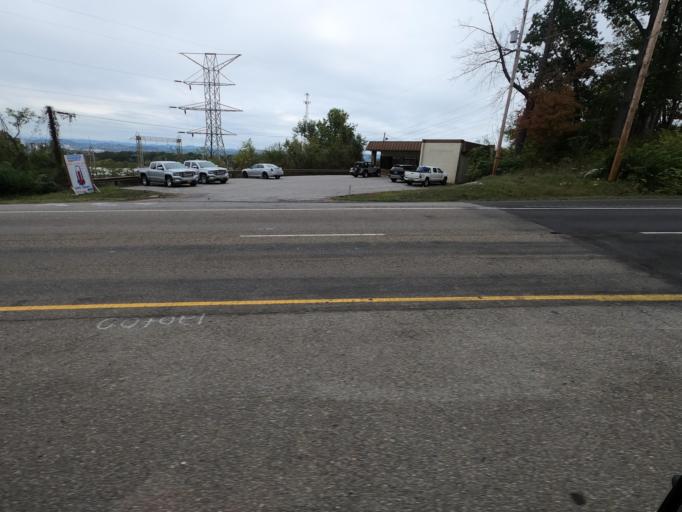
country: US
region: Tennessee
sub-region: Sullivan County
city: Colonial Heights
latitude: 36.5176
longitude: -82.5275
